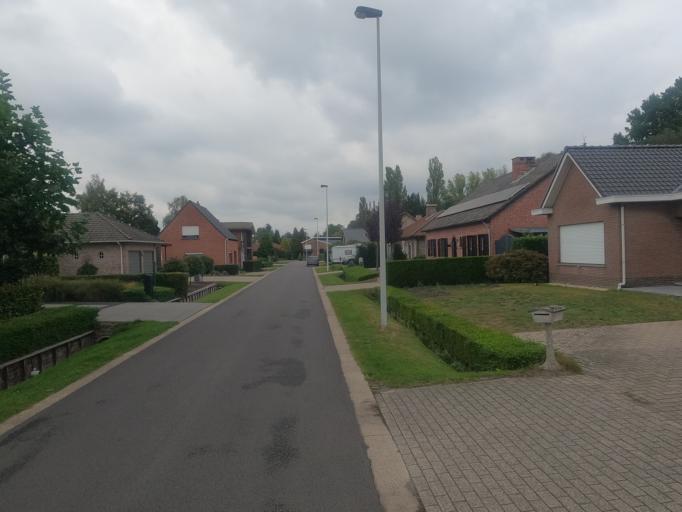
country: BE
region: Flanders
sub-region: Provincie Antwerpen
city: Lier
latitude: 51.1410
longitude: 4.6165
